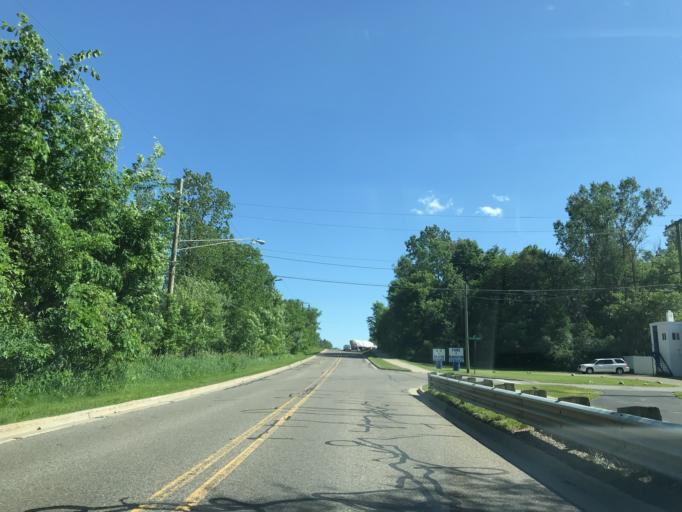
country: US
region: Michigan
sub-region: Oakland County
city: Novi
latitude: 42.5061
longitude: -83.4767
